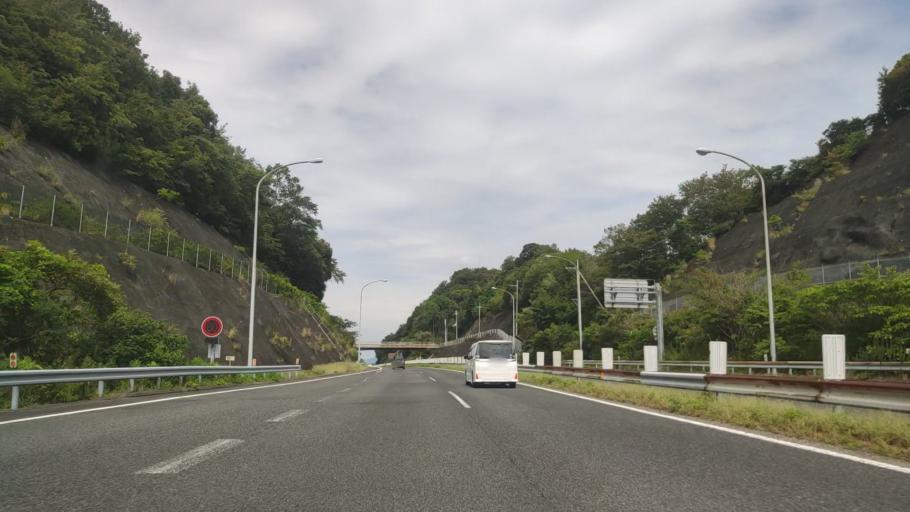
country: JP
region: Wakayama
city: Kainan
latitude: 34.1595
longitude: 135.2323
